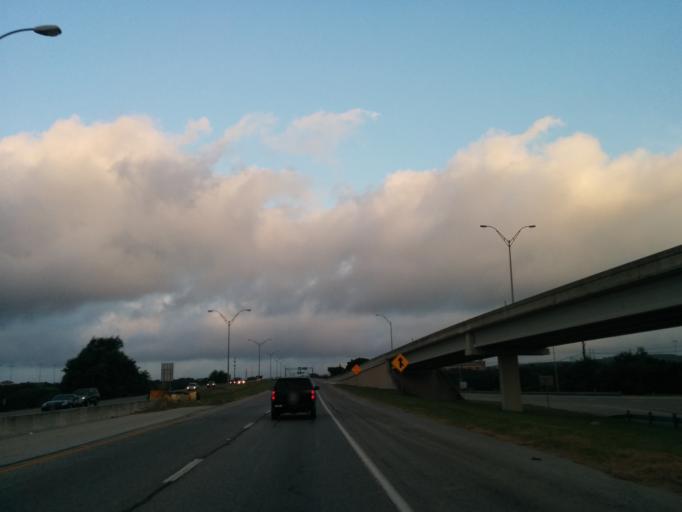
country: US
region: Texas
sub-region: Bexar County
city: Shavano Park
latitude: 29.5891
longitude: -98.6152
